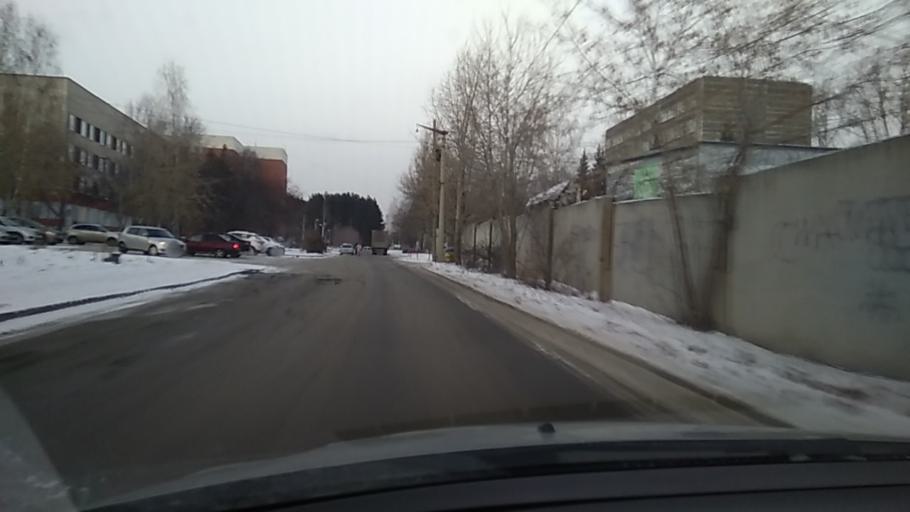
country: RU
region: Sverdlovsk
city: Istok
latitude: 56.7608
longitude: 60.7166
